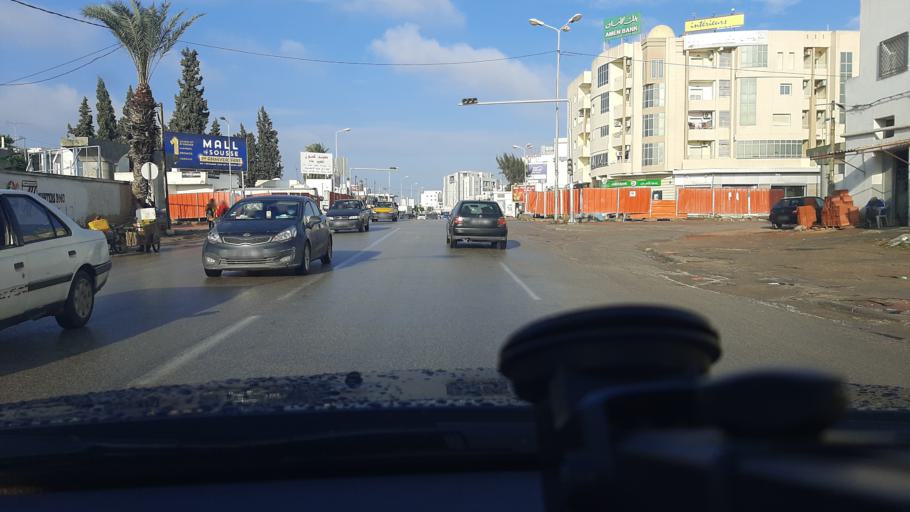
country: TN
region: Safaqis
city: Sfax
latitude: 34.7458
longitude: 10.7267
